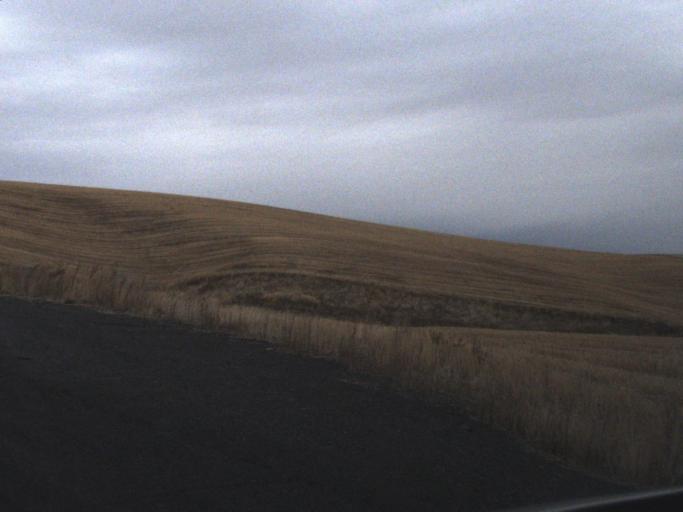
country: US
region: Washington
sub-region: Adams County
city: Ritzville
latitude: 46.7913
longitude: -118.3881
